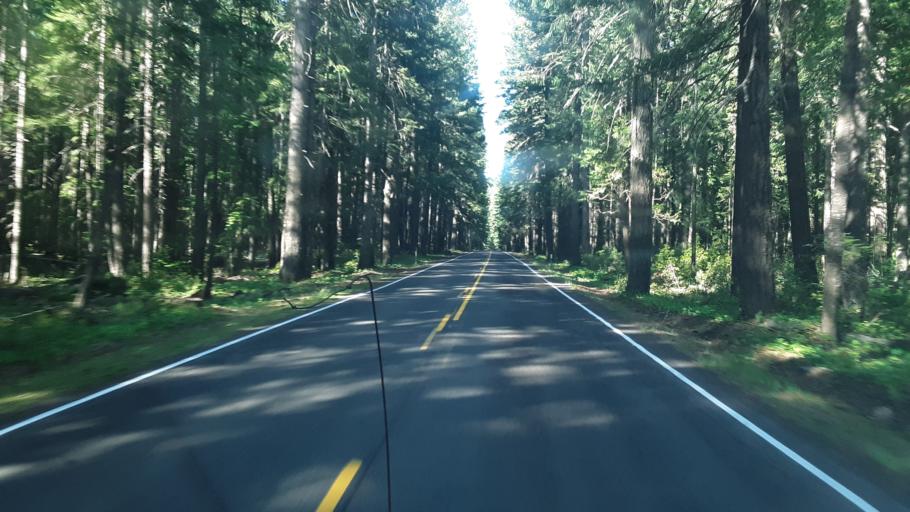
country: US
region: Oregon
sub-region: Jackson County
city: Shady Cove
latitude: 42.9453
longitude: -122.4142
